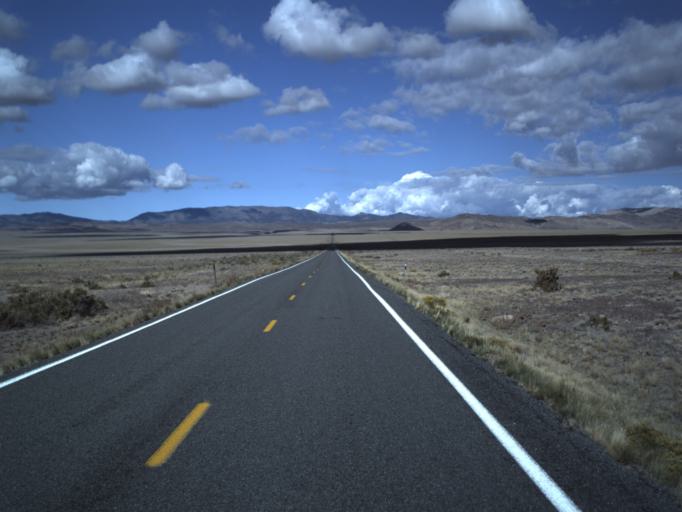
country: US
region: Utah
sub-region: Beaver County
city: Milford
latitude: 38.5443
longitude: -113.7143
